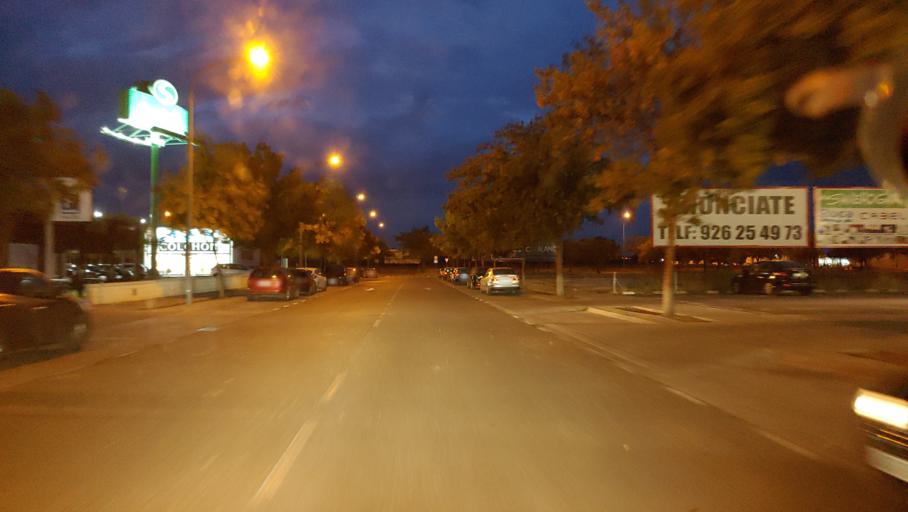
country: ES
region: Castille-La Mancha
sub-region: Provincia de Ciudad Real
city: Ciudad Real
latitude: 38.9857
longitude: -3.9076
